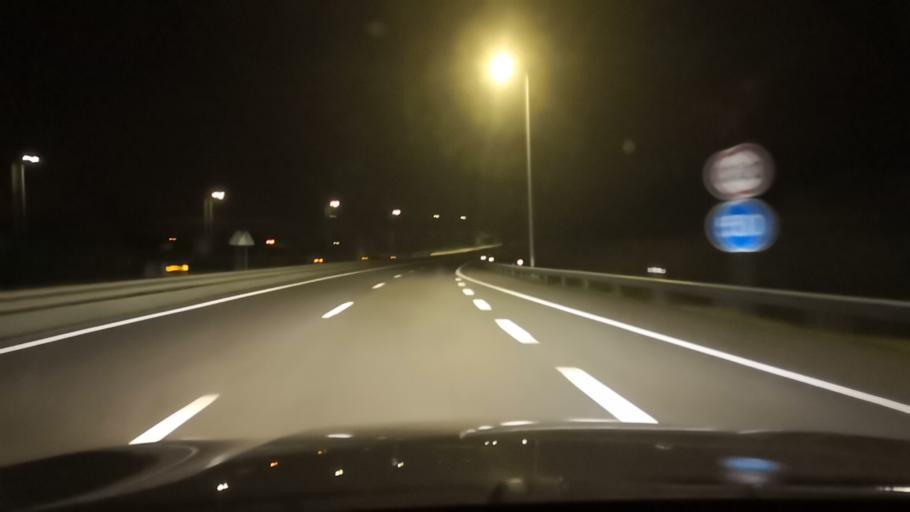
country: PT
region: Setubal
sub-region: Palmela
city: Palmela
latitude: 38.5826
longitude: -8.8634
